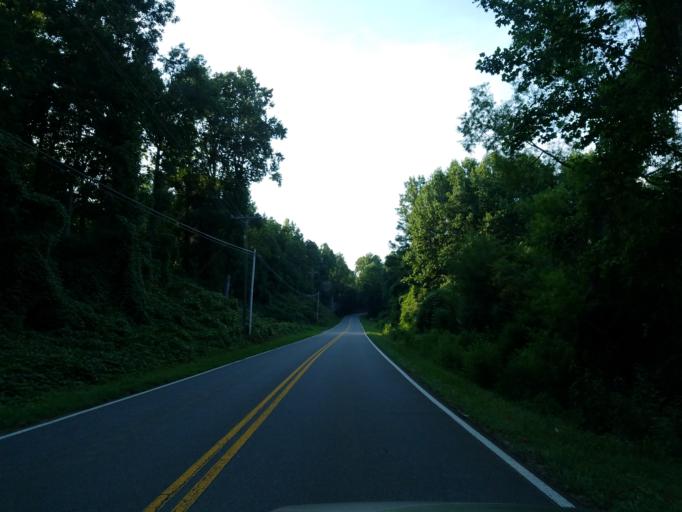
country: US
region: Georgia
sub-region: Pickens County
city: Jasper
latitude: 34.5431
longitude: -84.5421
